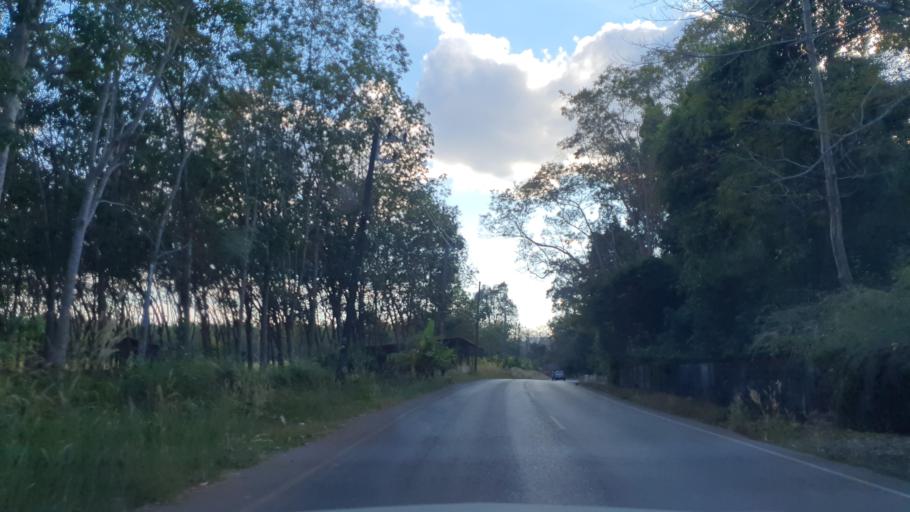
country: TH
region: Changwat Bueng Kan
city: Si Wilai
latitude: 18.1343
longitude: 103.8859
